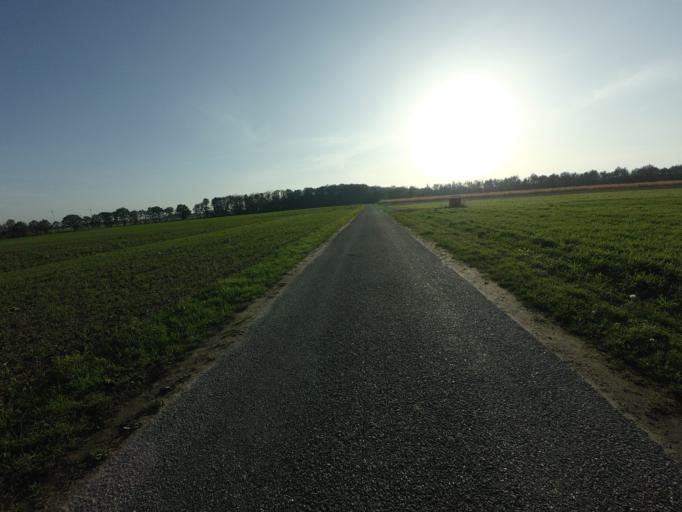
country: NL
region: Limburg
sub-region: Gemeente Echt-Susteren
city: Koningsbosch
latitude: 51.0724
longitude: 5.9579
